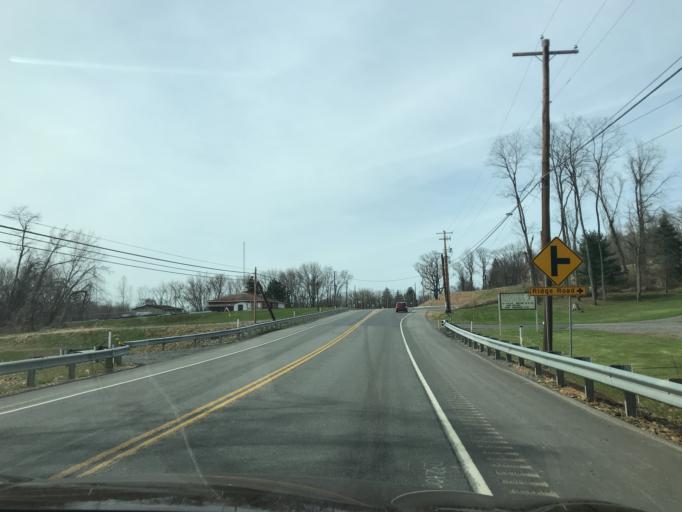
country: US
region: Pennsylvania
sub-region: Northumberland County
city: Northumberland
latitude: 40.9162
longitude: -76.8416
